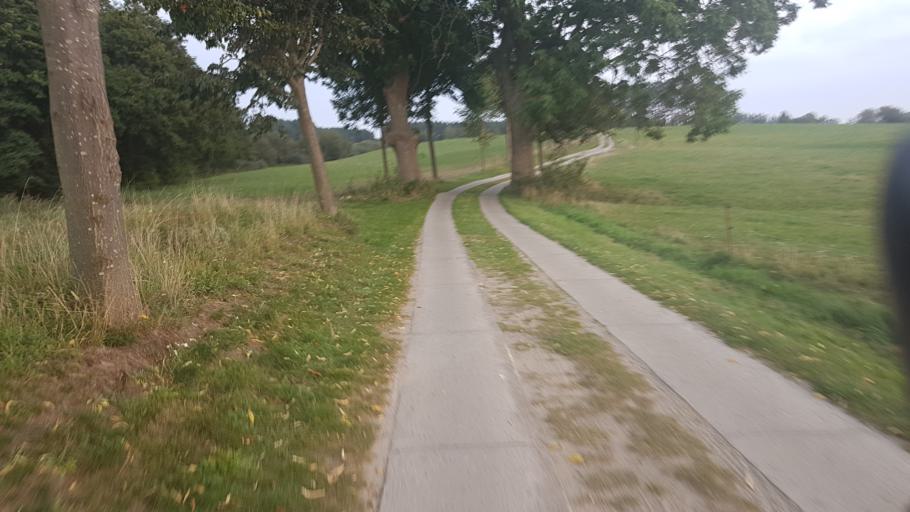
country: DE
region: Mecklenburg-Vorpommern
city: Putbus
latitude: 54.3516
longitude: 13.5287
